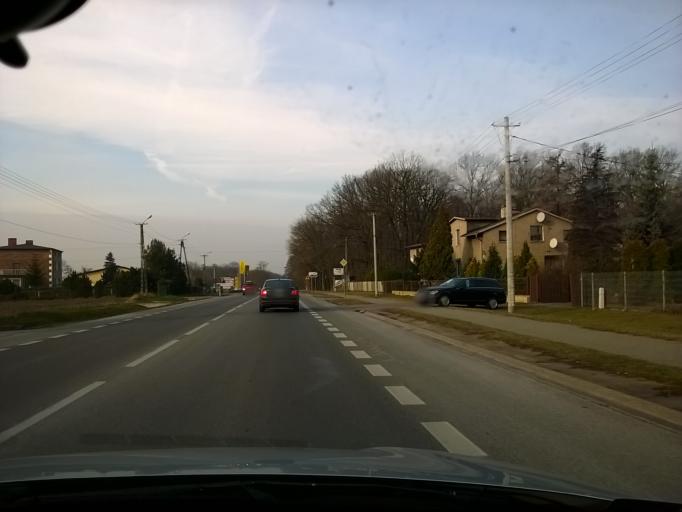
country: PL
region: Silesian Voivodeship
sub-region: Powiat gliwicki
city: Przyszowice
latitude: 50.2424
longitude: 18.7610
